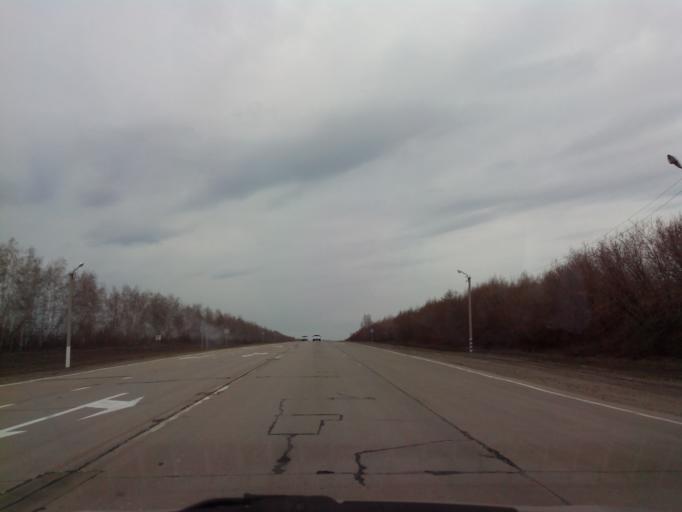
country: RU
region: Tambov
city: Znamenka
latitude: 52.4031
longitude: 41.3898
